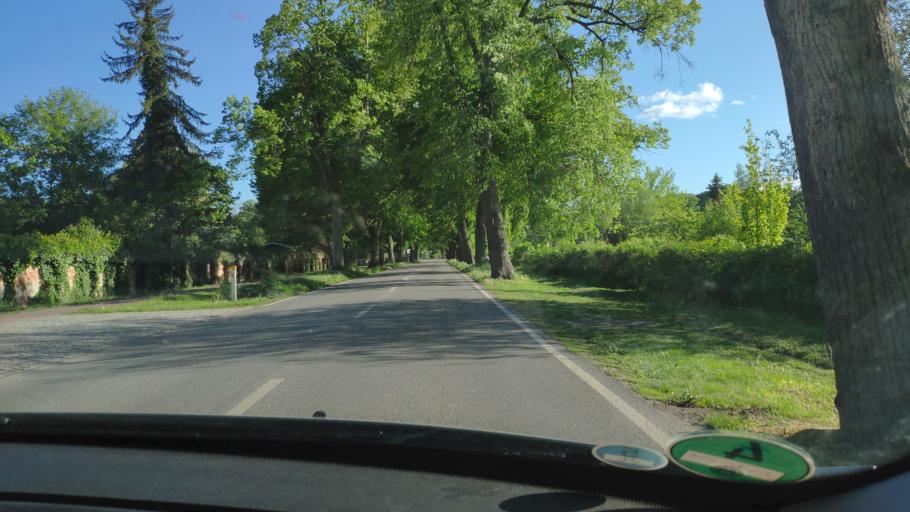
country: DE
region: Mecklenburg-Vorpommern
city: Neustrelitz
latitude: 53.3589
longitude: 13.0514
